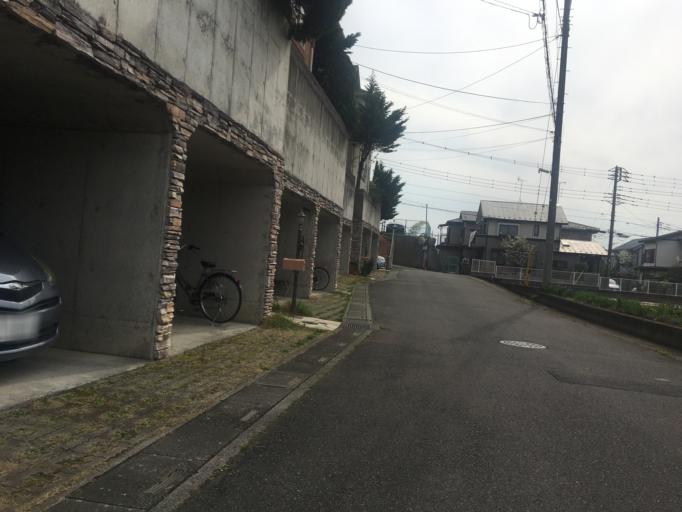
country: JP
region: Saitama
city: Shiki
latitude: 35.8141
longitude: 139.5562
